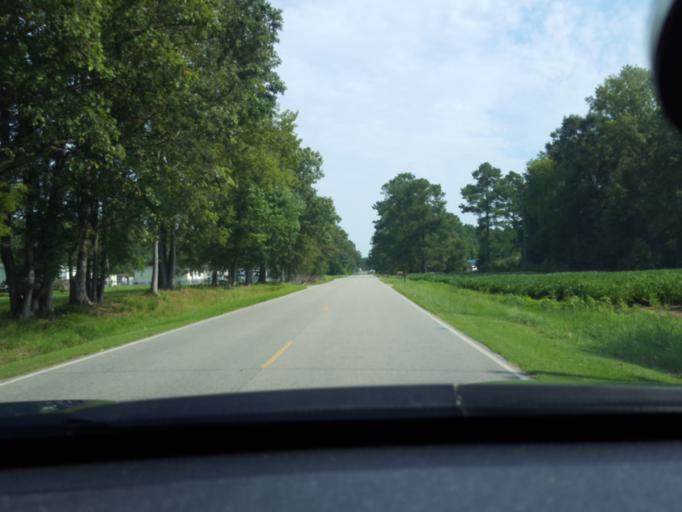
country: US
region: North Carolina
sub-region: Washington County
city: Plymouth
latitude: 35.8860
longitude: -76.7072
